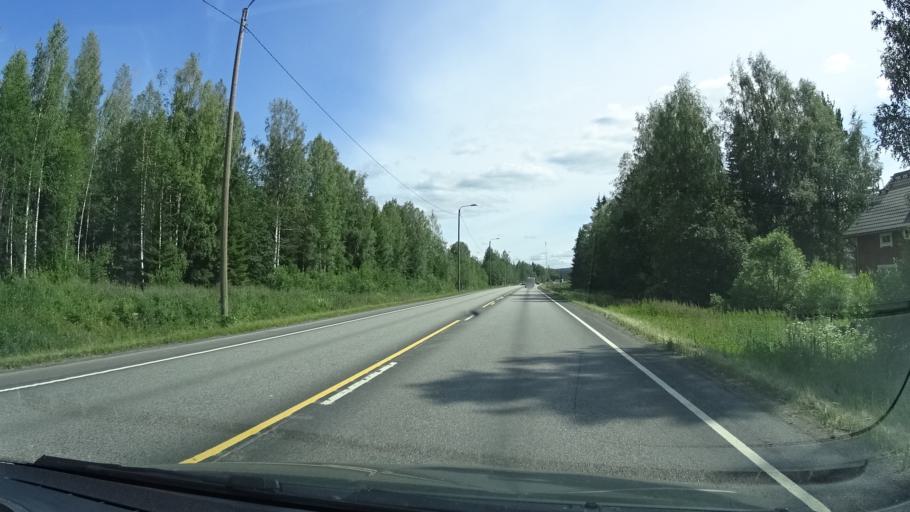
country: FI
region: Central Finland
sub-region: Jyvaeskylae
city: Uurainen
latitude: 62.2657
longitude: 25.4527
